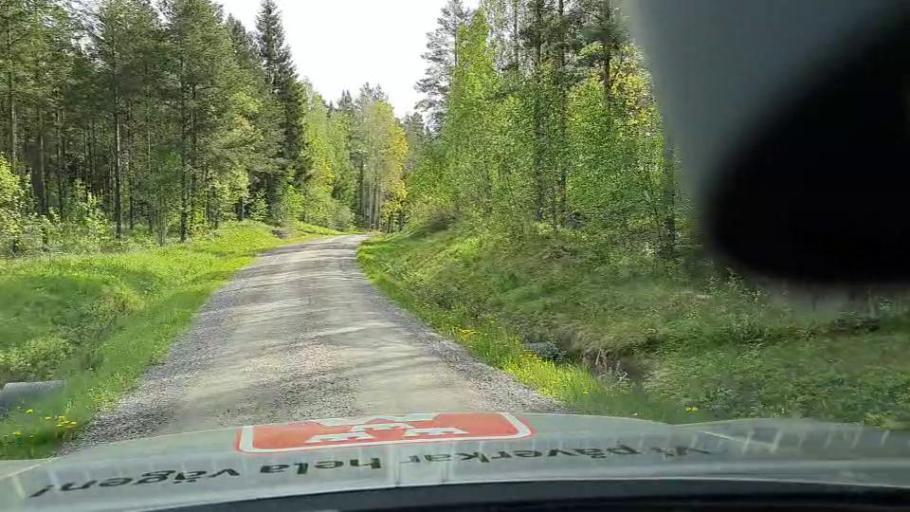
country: SE
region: Soedermanland
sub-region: Eskilstuna Kommun
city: Arla
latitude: 59.2615
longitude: 16.8361
